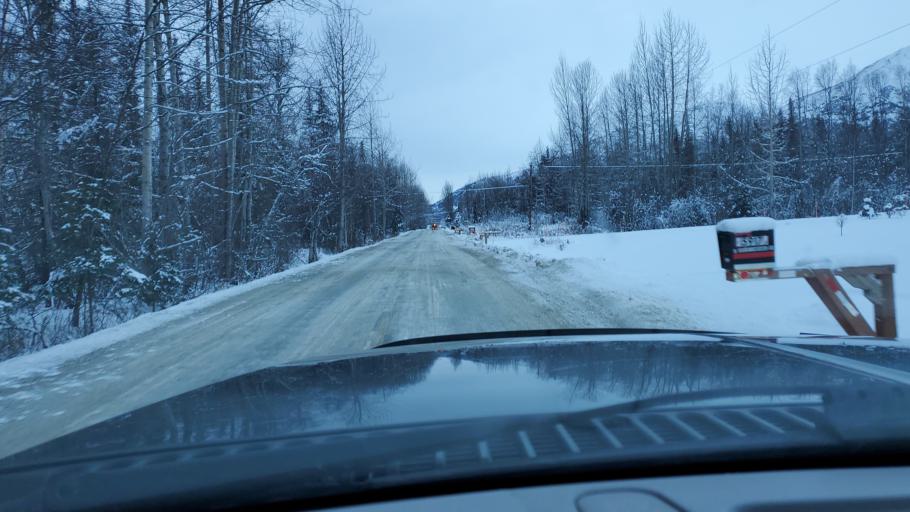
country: US
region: Alaska
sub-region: Matanuska-Susitna Borough
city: Fishhook
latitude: 61.6933
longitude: -149.3014
